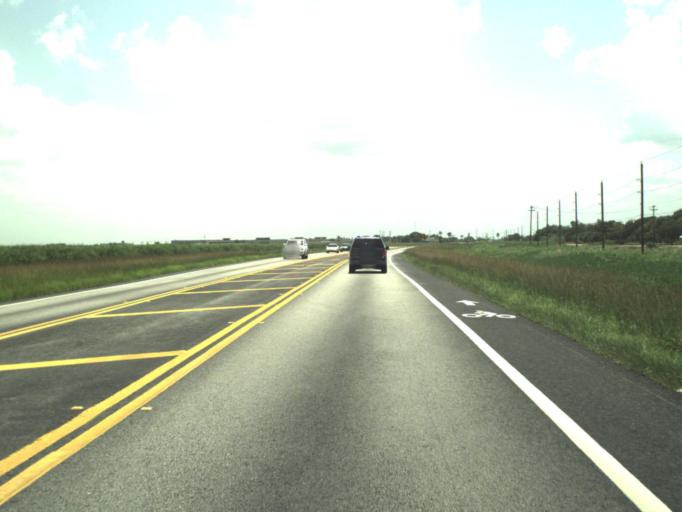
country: US
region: Florida
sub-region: Palm Beach County
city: Belle Glade
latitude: 26.7364
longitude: -80.6634
